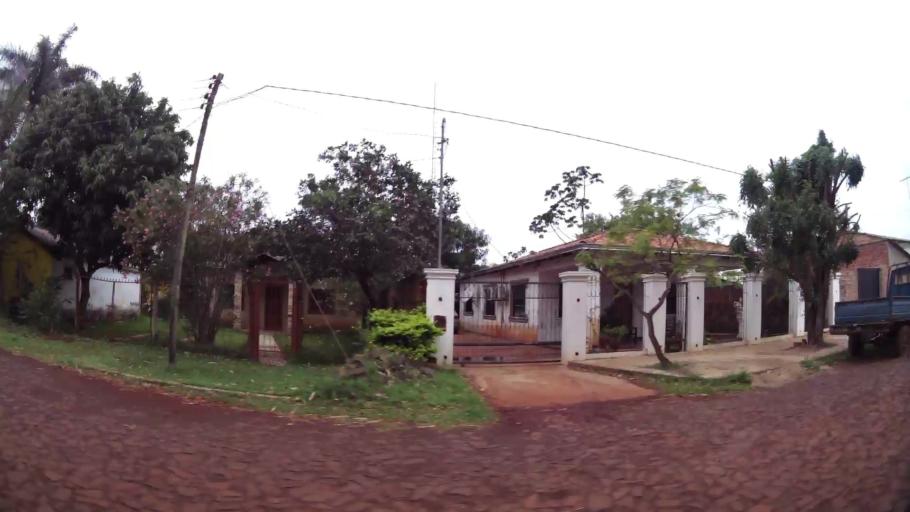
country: PY
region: Alto Parana
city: Ciudad del Este
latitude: -25.4026
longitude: -54.6378
